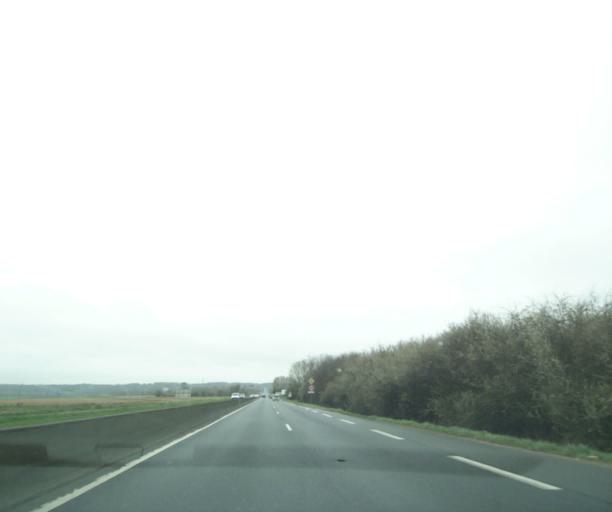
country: FR
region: Ile-de-France
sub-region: Departement de l'Essonne
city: Boissy-sous-Saint-Yon
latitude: 48.5585
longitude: 2.2245
